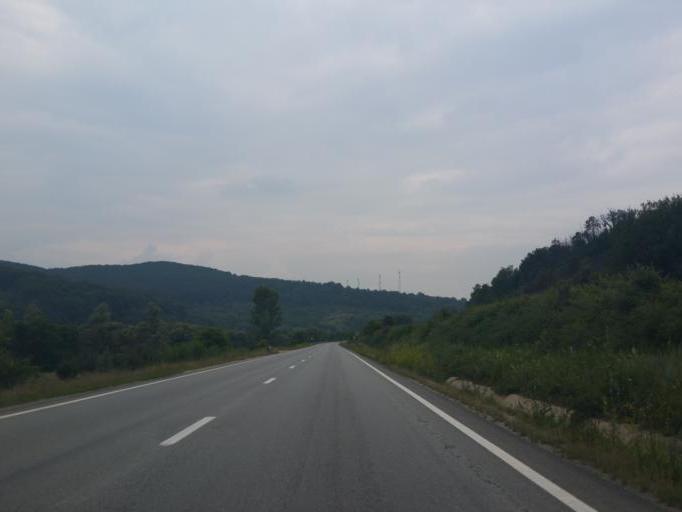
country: RO
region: Salaj
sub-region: Comuna Zimbor
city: Zimbor
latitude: 46.9720
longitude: 23.2619
